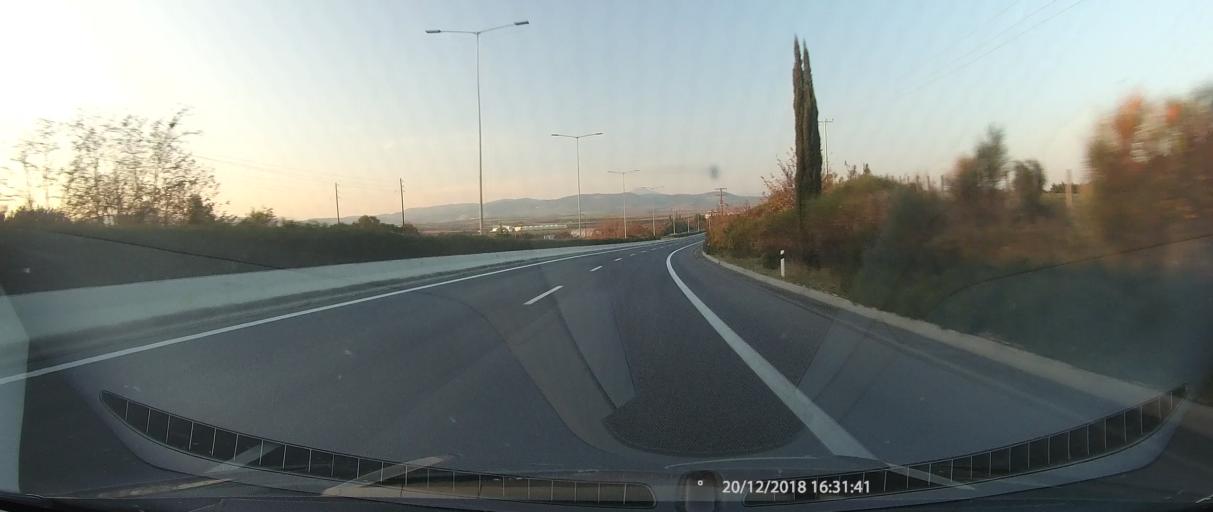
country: GR
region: Thessaly
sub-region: Nomos Magnisias
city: Evxinoupolis
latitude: 39.2303
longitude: 22.7380
